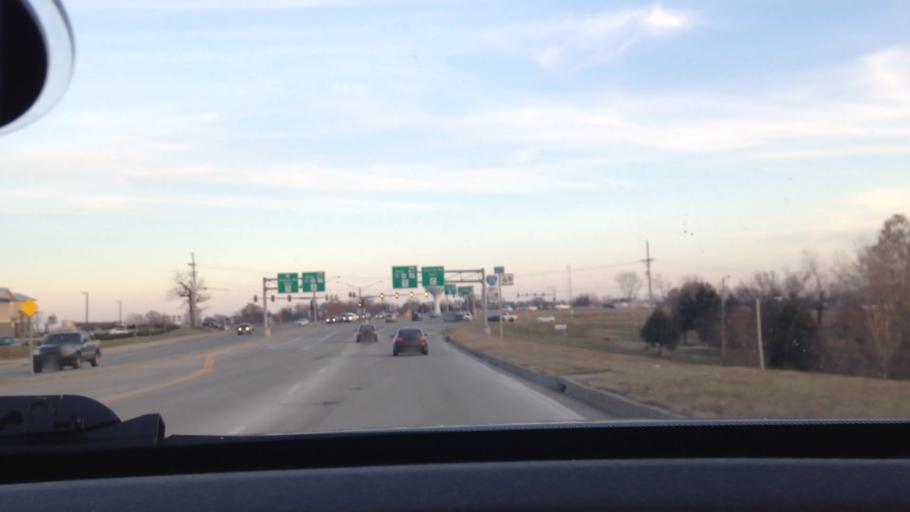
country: US
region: Missouri
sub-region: Clay County
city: Liberty
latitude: 39.2670
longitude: -94.4503
